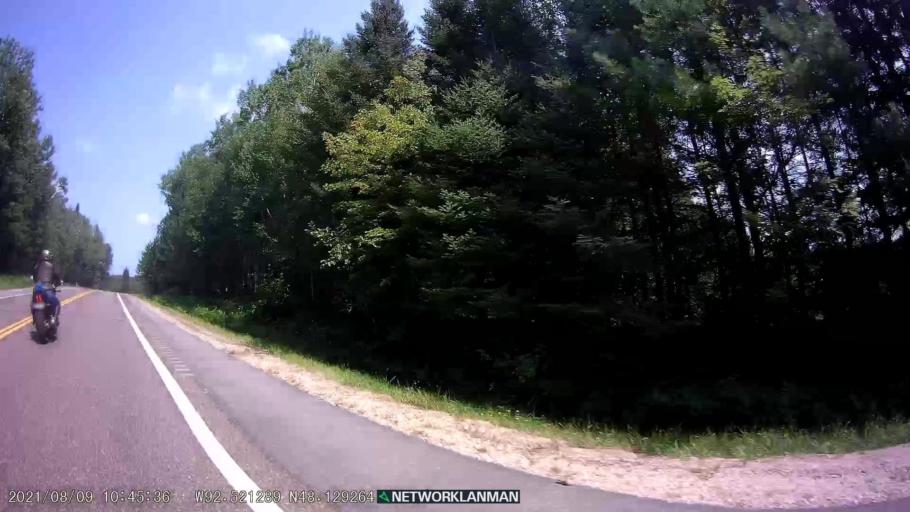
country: US
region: Minnesota
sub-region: Saint Louis County
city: Parkville
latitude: 48.1296
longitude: -92.5213
